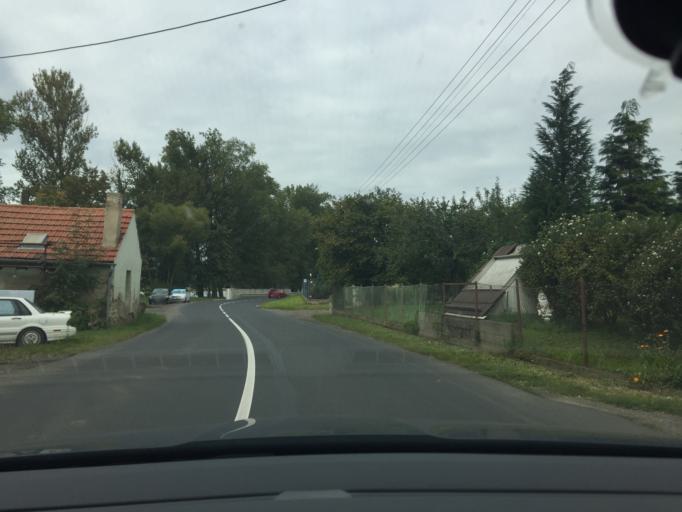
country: CZ
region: Ustecky
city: Kresice
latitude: 50.5094
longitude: 14.2270
